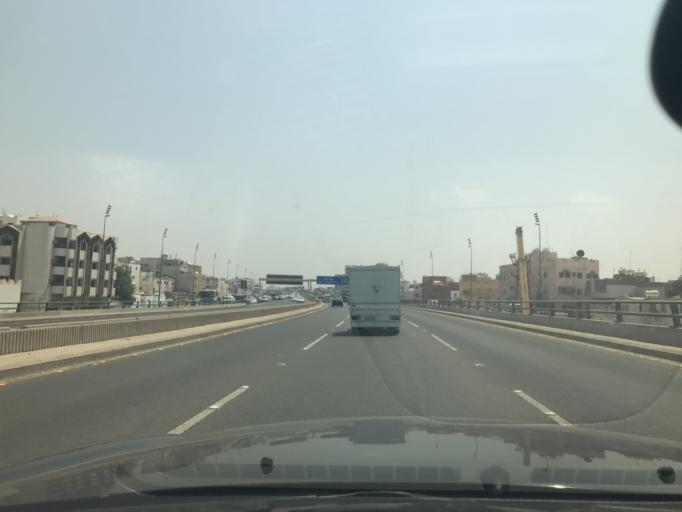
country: SA
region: Makkah
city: Jeddah
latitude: 21.4773
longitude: 39.1889
